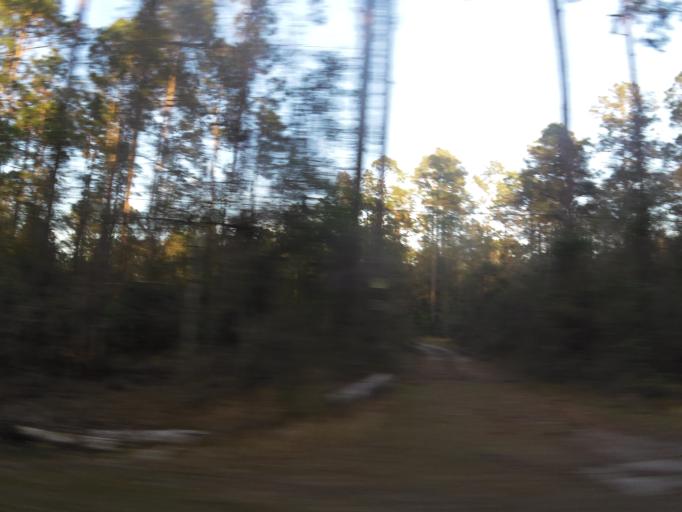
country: US
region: Florida
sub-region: Clay County
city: Green Cove Springs
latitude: 29.8881
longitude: -81.5648
